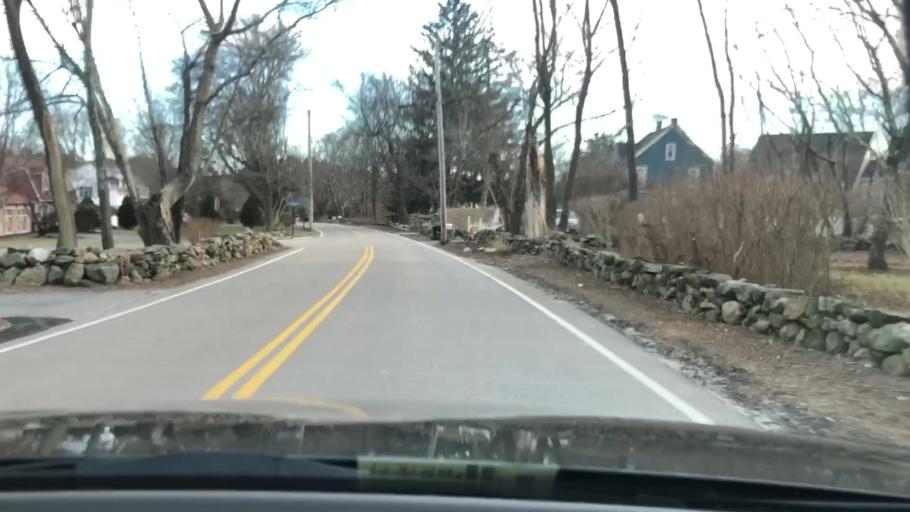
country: US
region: Massachusetts
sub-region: Worcester County
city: Blackstone
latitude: 42.0472
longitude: -71.5299
